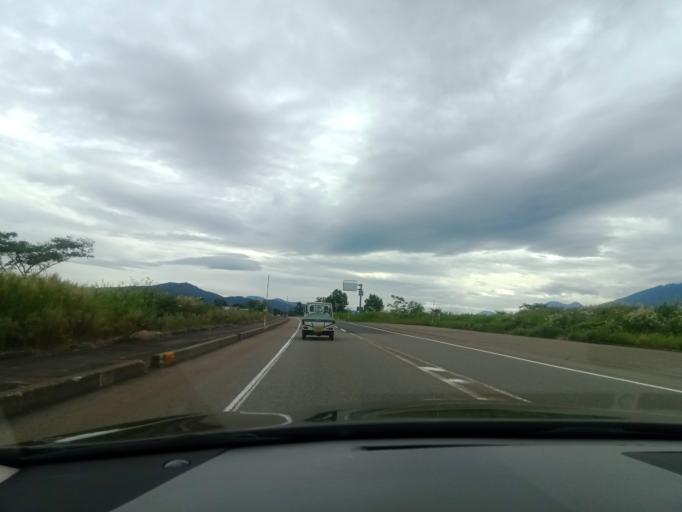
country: JP
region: Niigata
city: Arai
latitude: 37.0227
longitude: 138.2271
